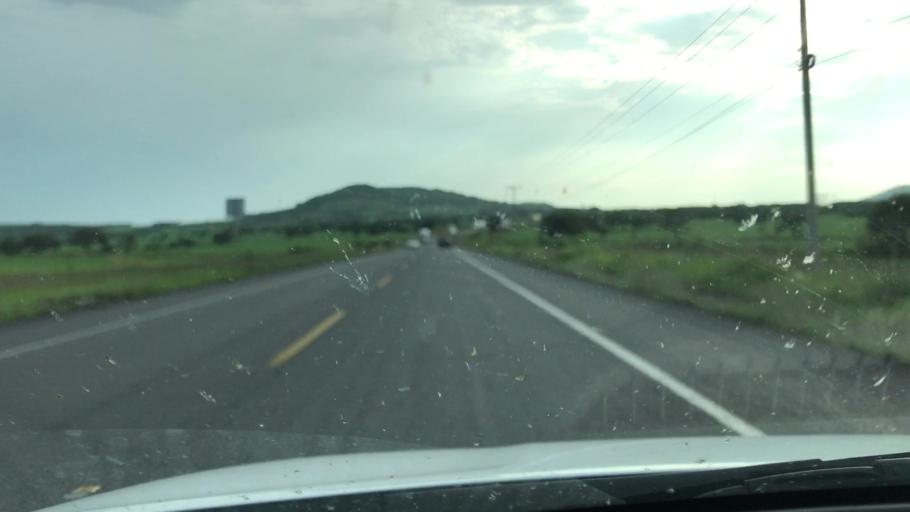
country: MX
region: Michoacan
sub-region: Yurecuaro
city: Yurecuaro
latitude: 20.3386
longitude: -102.1851
